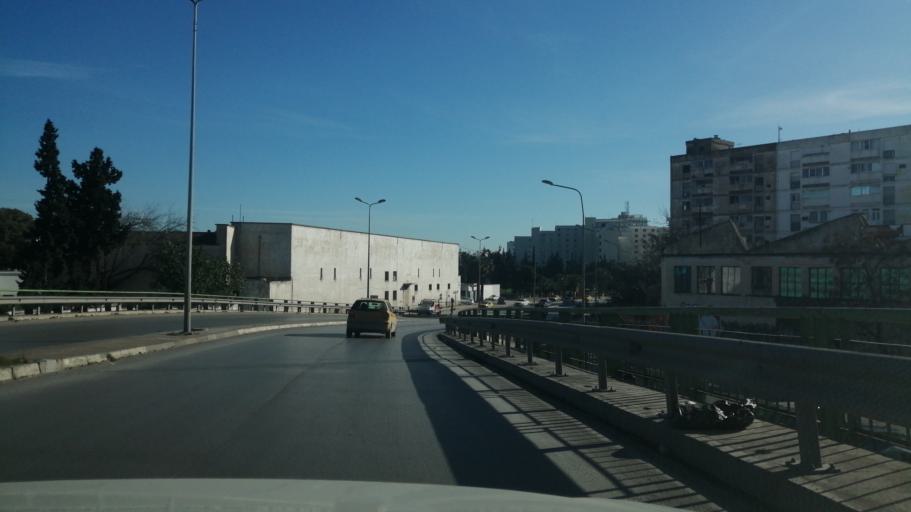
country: TN
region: Tunis
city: Tunis
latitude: 36.8135
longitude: 10.1697
